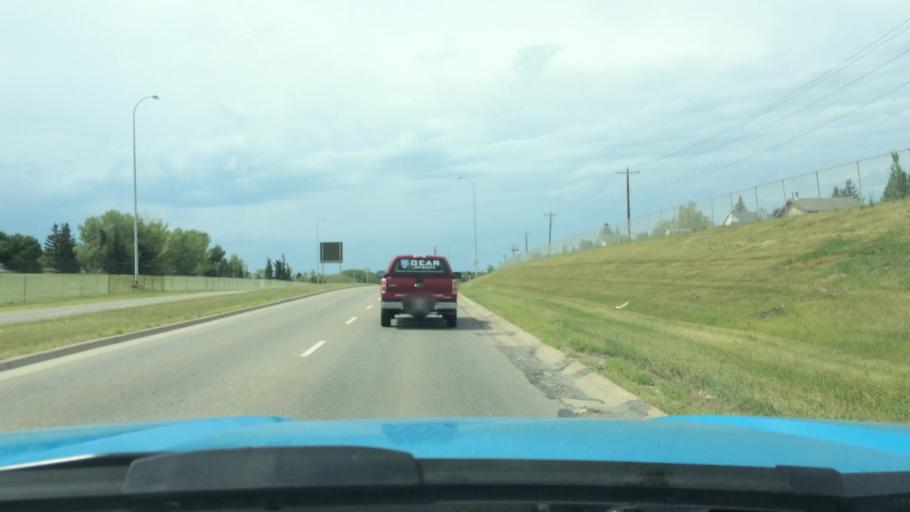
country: CA
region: Alberta
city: Calgary
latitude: 51.1173
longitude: -114.1593
